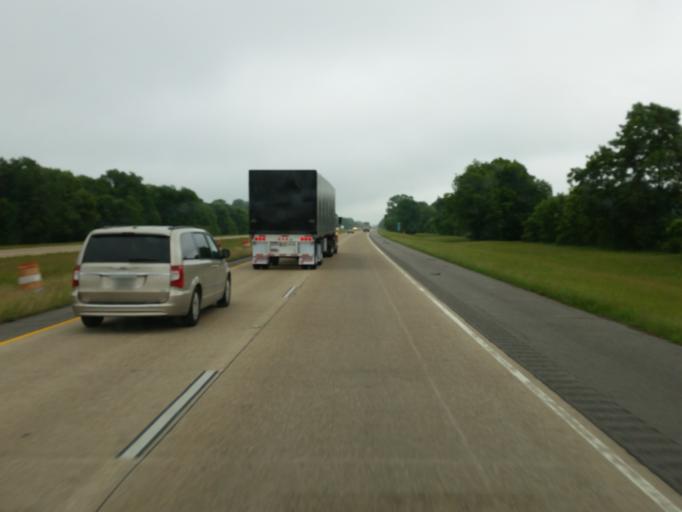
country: US
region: Louisiana
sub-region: Madison Parish
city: Tallulah
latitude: 32.3601
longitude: -91.1102
